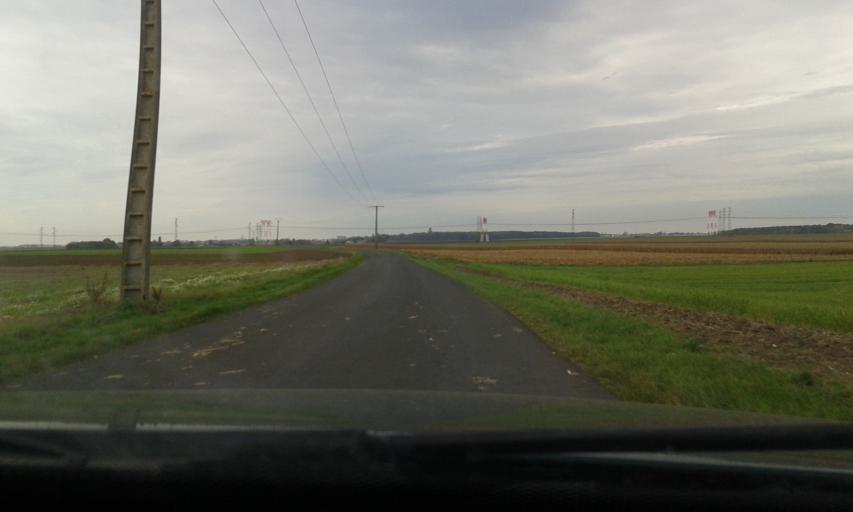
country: FR
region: Centre
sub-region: Departement du Loiret
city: Gidy
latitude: 47.9903
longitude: 1.8321
